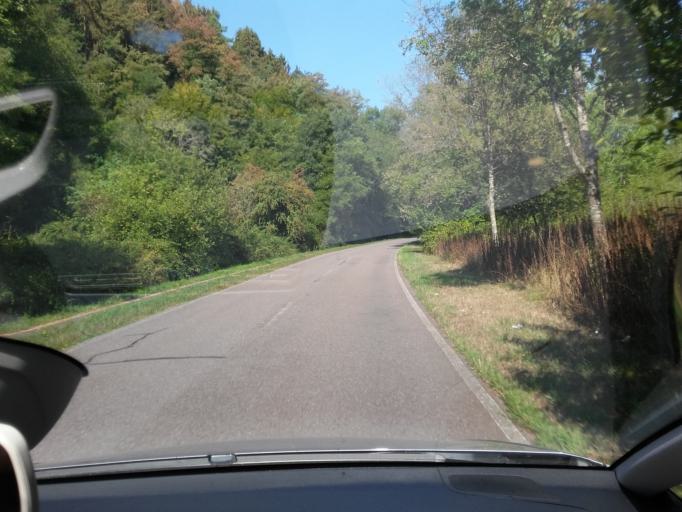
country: DE
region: Saarland
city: Mettlach
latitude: 49.4751
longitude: 6.5828
